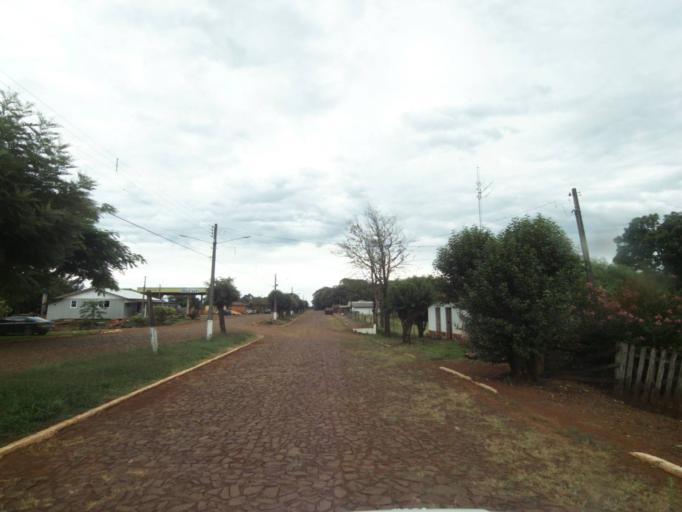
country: BR
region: Parana
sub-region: Guaraniacu
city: Guaraniacu
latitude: -24.9190
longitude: -52.9381
